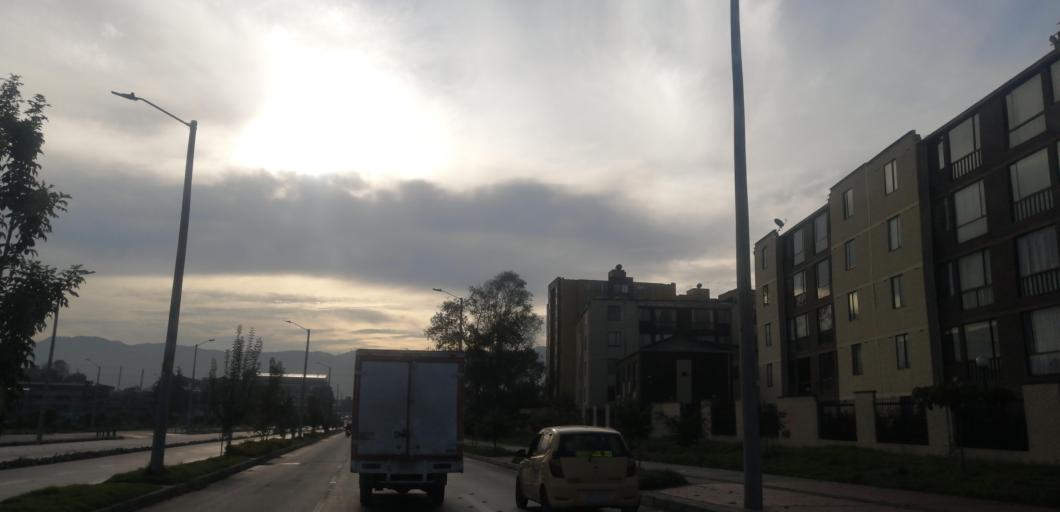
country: CO
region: Bogota D.C.
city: Bogota
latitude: 4.6369
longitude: -74.1264
